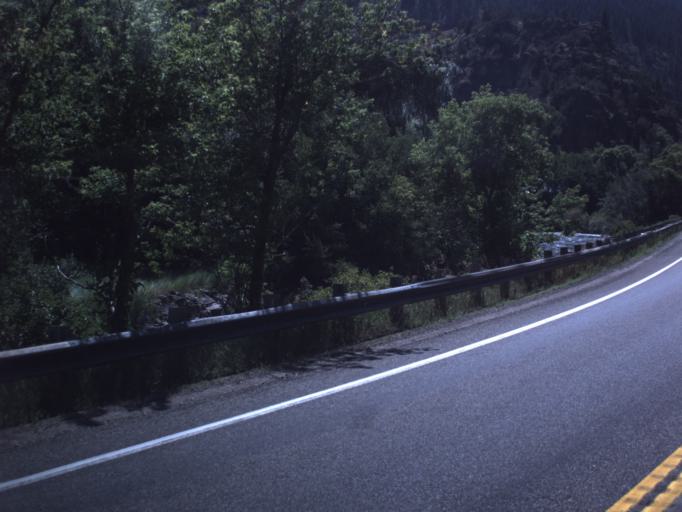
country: US
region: Utah
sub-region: Cache County
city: North Logan
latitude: 41.7684
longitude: -111.6631
